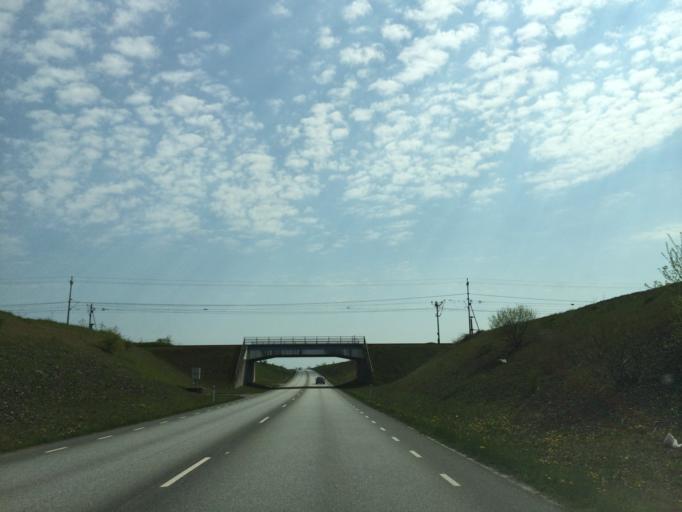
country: SE
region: Skane
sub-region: Staffanstorps Kommun
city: Hjaerup
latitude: 55.6865
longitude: 13.1556
